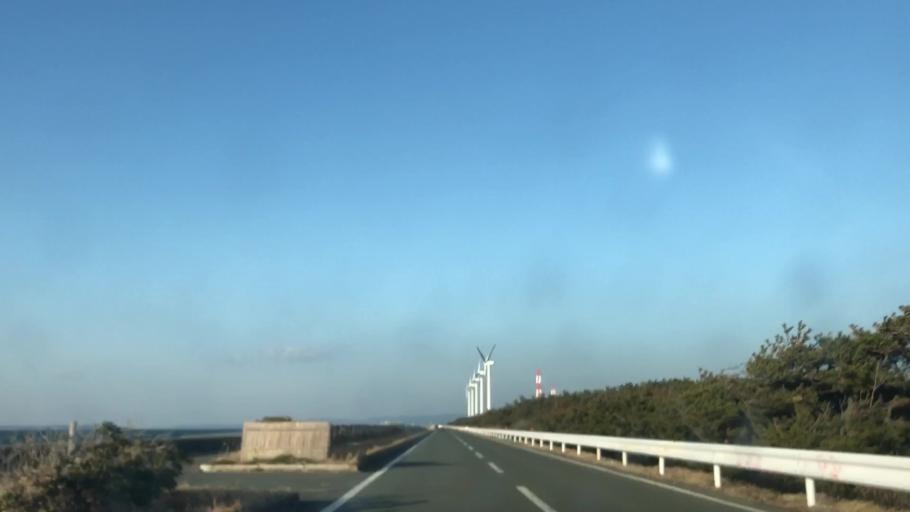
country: JP
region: Aichi
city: Toyohama
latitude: 34.6296
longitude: 137.0476
